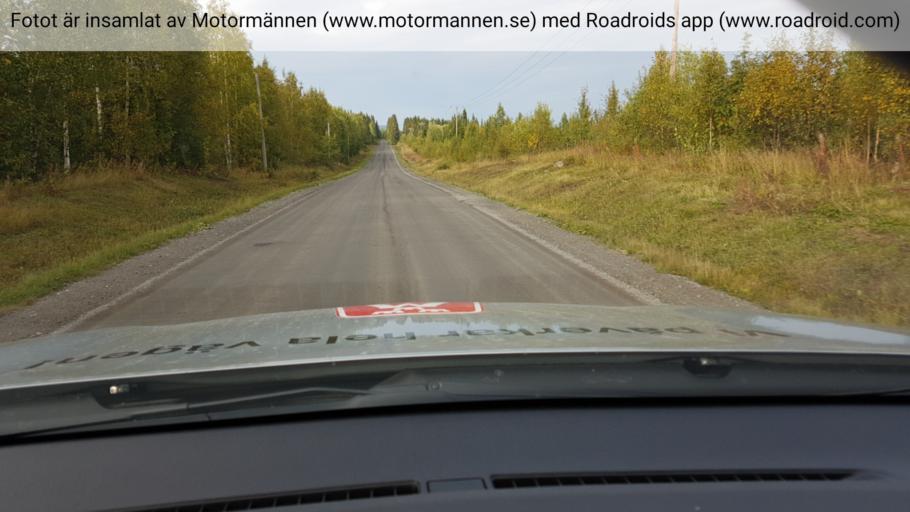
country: SE
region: Jaemtland
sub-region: Stroemsunds Kommun
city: Stroemsund
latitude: 63.9938
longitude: 15.8165
